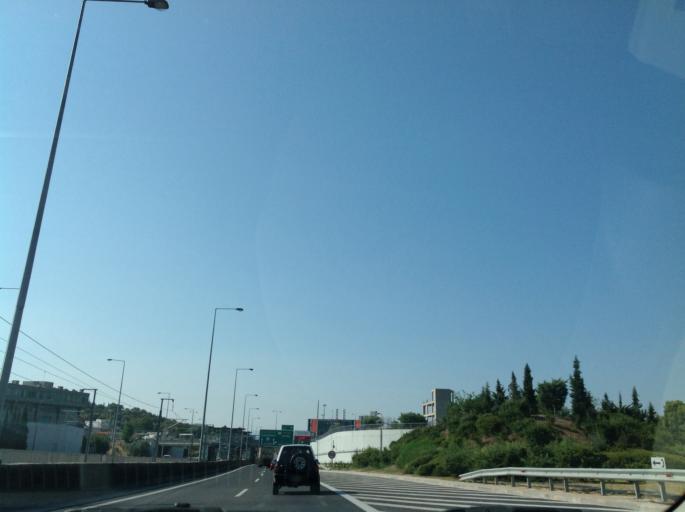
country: GR
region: Attica
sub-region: Nomarchia Anatolikis Attikis
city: Pallini
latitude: 38.0080
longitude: 23.8686
